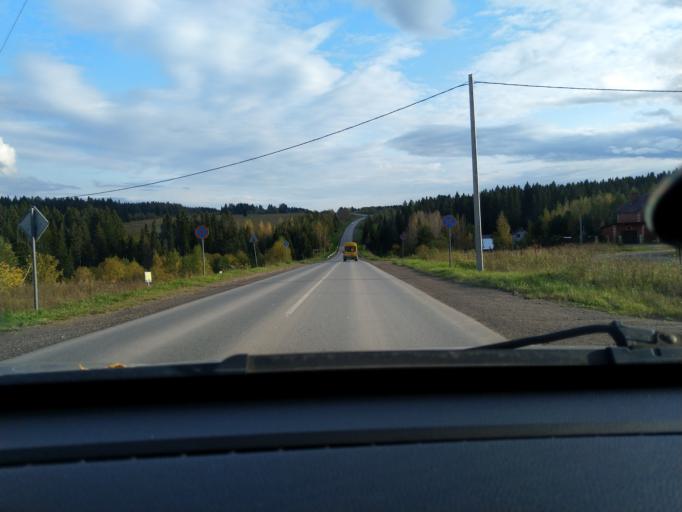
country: RU
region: Perm
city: Polazna
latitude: 58.2815
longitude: 56.4123
